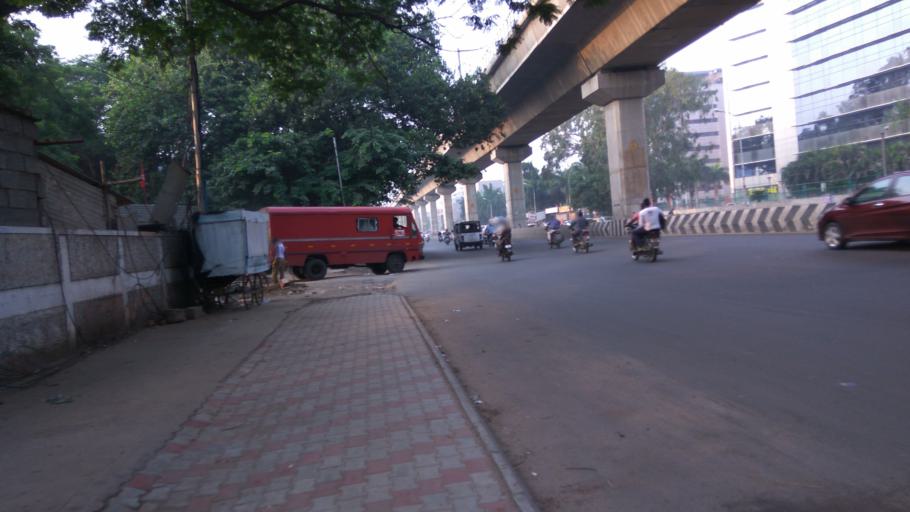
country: IN
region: Tamil Nadu
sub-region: Kancheepuram
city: Alandur
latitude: 13.0159
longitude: 80.2053
